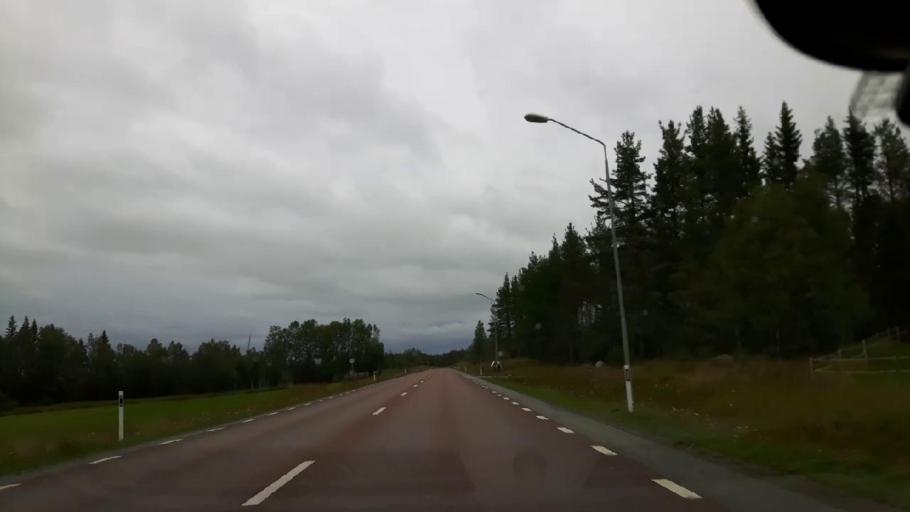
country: SE
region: Jaemtland
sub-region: Bergs Kommun
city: Hoverberg
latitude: 62.9316
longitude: 14.5384
